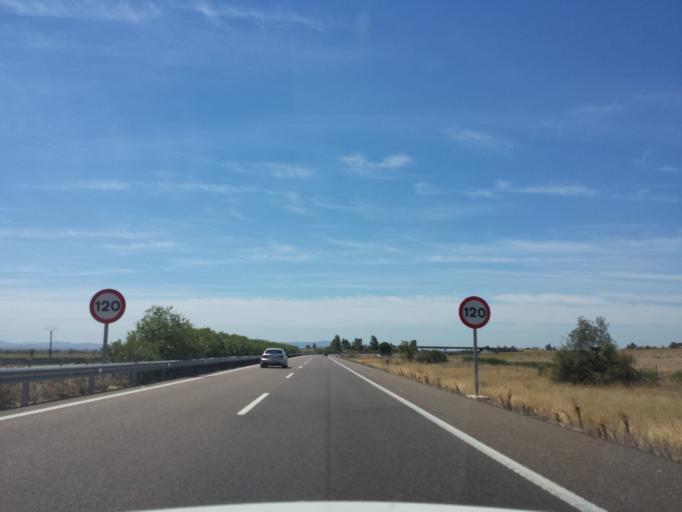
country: ES
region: Extremadura
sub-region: Provincia de Badajoz
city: Santa Amalia
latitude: 38.9989
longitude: -6.0940
